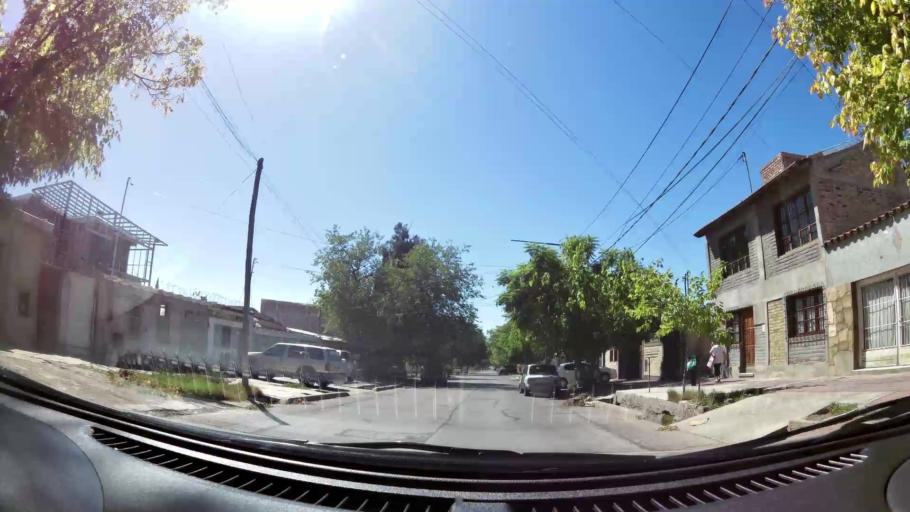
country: AR
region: Mendoza
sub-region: Departamento de Godoy Cruz
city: Godoy Cruz
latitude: -32.9047
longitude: -68.8641
